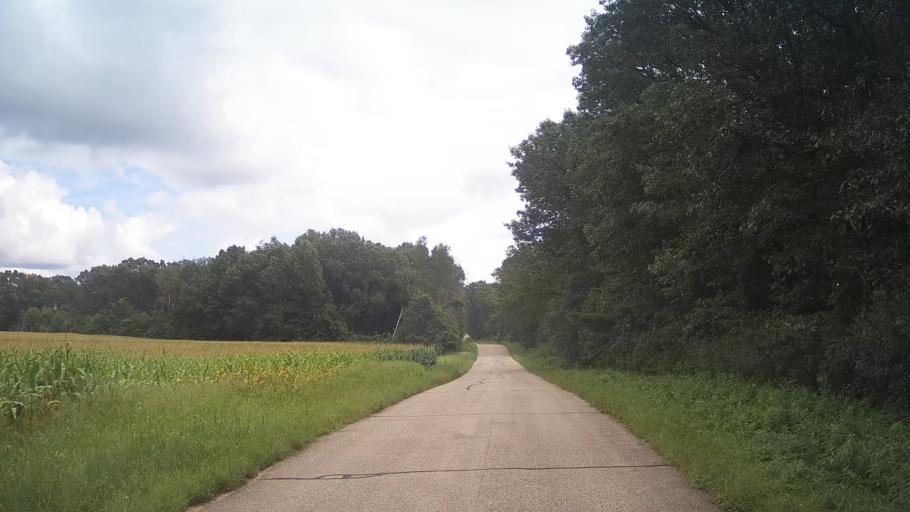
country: US
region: Wisconsin
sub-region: Adams County
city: Friendship
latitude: 44.0278
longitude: -89.9098
